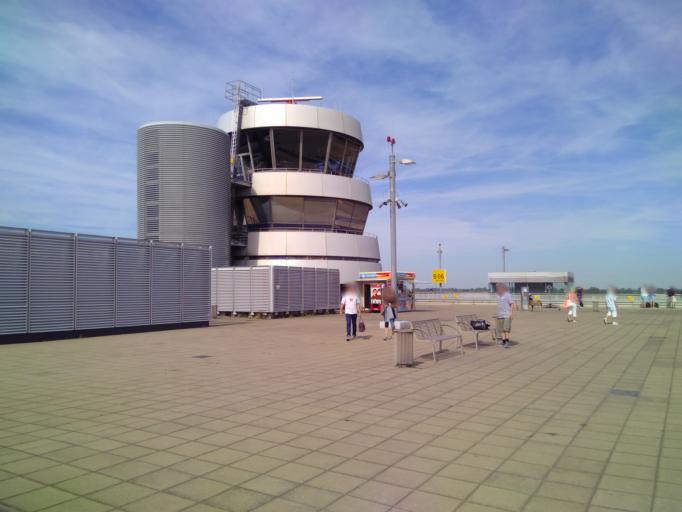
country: DE
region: North Rhine-Westphalia
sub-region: Regierungsbezirk Dusseldorf
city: Dusseldorf
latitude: 51.2799
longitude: 6.7634
